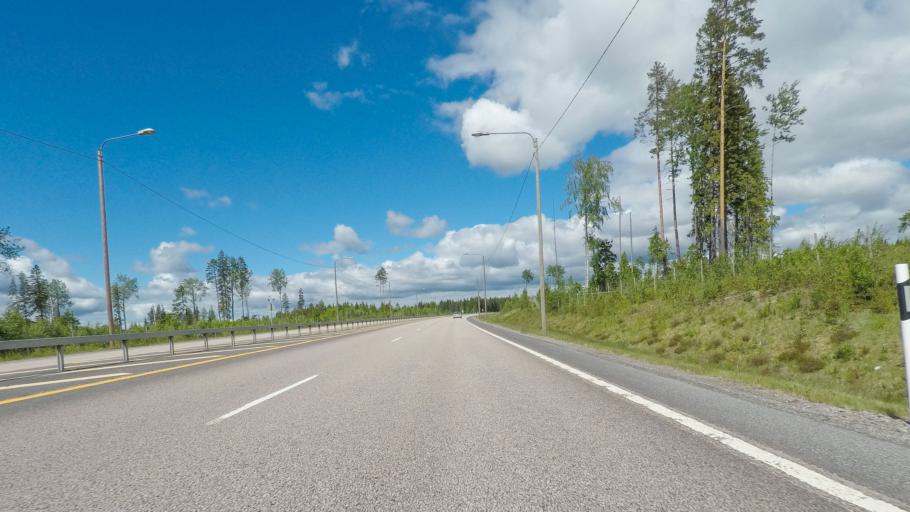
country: FI
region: Paijanne Tavastia
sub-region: Lahti
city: Heinola
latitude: 61.3567
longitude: 26.0428
